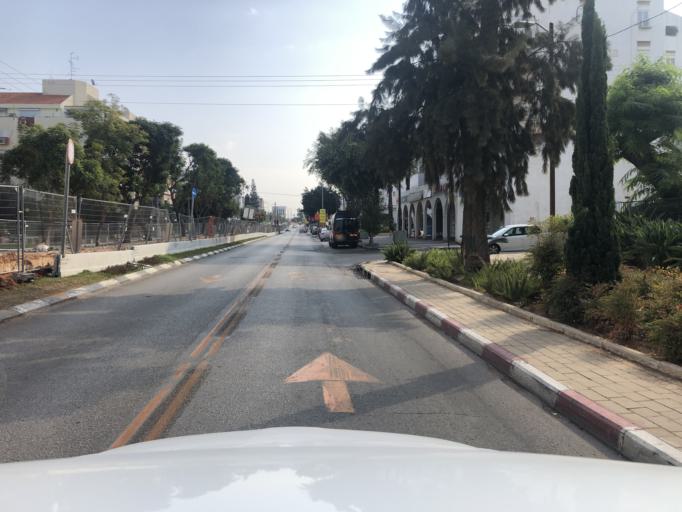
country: IL
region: Central District
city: Kfar Saba
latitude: 32.1732
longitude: 34.9175
